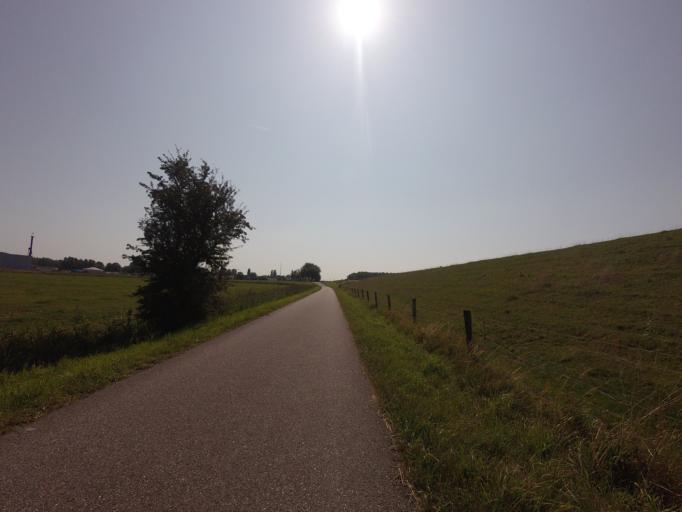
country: NL
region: Groningen
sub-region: Gemeente De Marne
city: Ulrum
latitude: 53.3464
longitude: 6.2974
